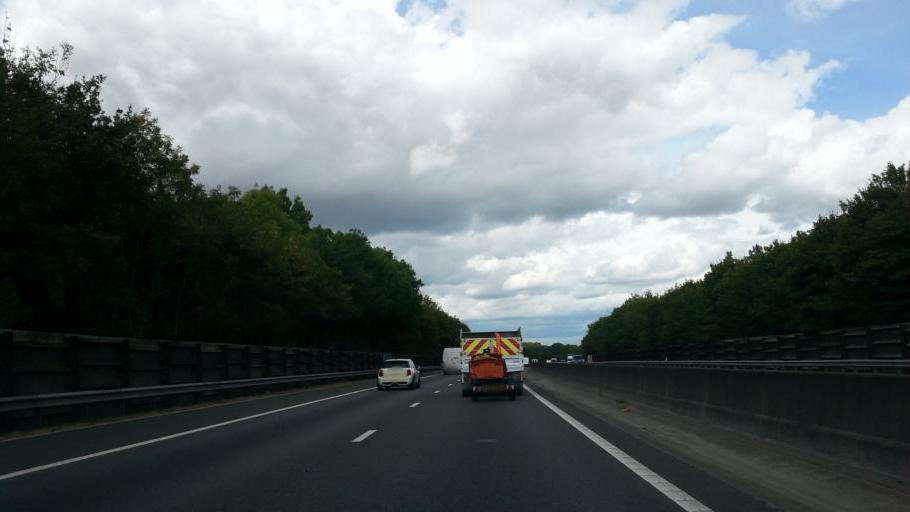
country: GB
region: England
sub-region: Essex
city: Elsenham
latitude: 51.9191
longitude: 0.2192
